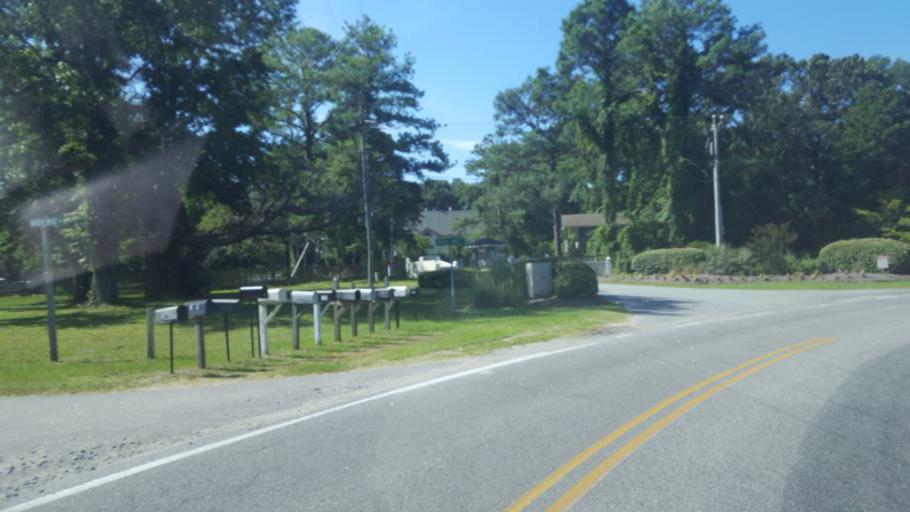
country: US
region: North Carolina
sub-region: Dare County
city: Kill Devil Hills
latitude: 36.0123
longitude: -75.6939
